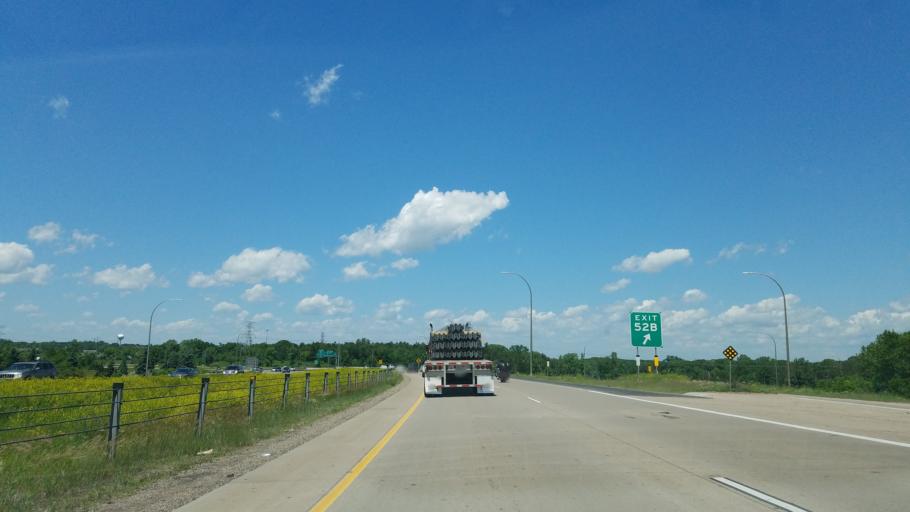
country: US
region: Minnesota
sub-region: Ramsey County
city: North Saint Paul
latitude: 45.0270
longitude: -92.9600
